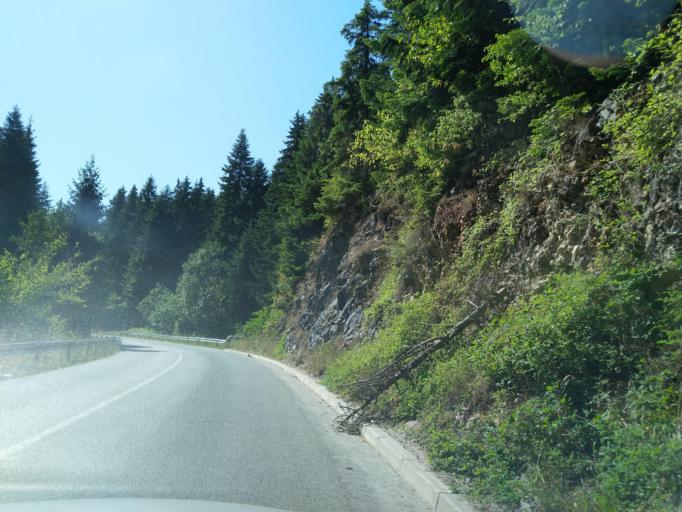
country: RS
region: Central Serbia
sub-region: Zlatiborski Okrug
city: Nova Varos
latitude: 43.4159
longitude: 19.8298
